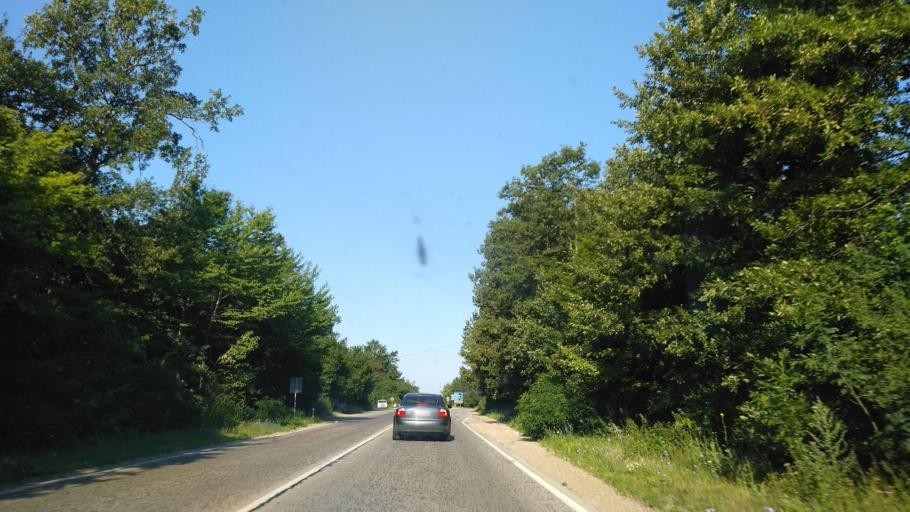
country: BG
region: Lovech
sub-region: Obshtina Lovech
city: Lovech
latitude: 43.0520
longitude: 24.8170
